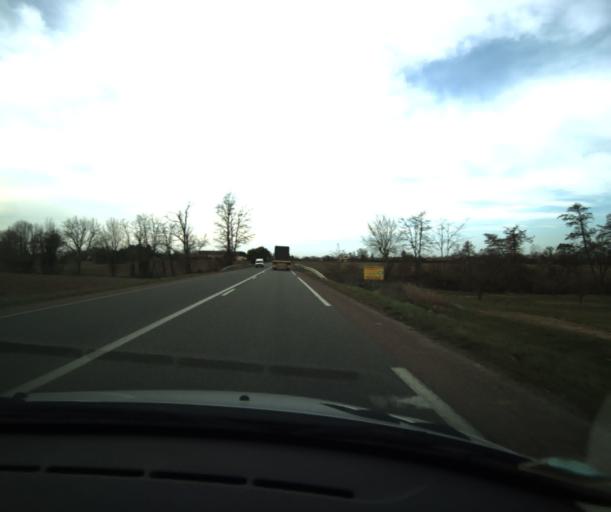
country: FR
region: Midi-Pyrenees
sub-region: Departement du Tarn-et-Garonne
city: Saint-Porquier
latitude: 43.9972
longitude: 1.1863
